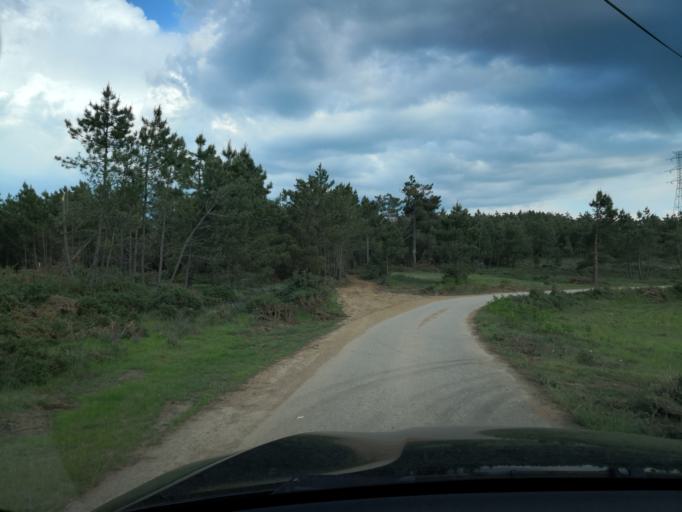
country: PT
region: Vila Real
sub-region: Sabrosa
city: Vilela
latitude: 41.2267
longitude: -7.6709
